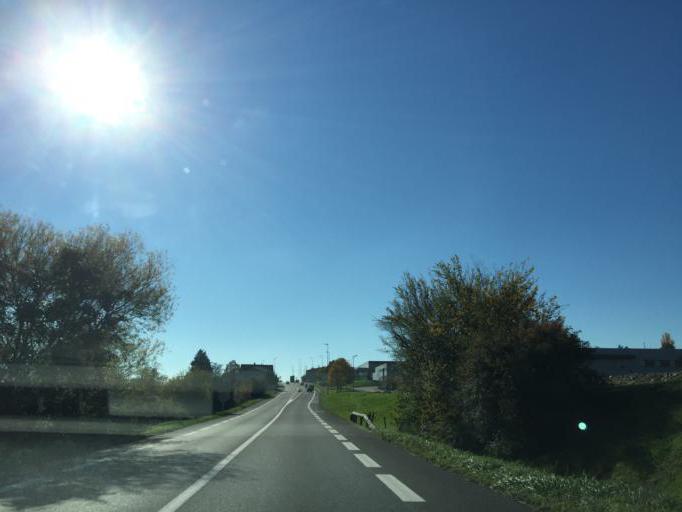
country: FR
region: Rhone-Alpes
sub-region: Departement du Rhone
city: Taluyers
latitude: 45.6364
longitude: 4.7349
